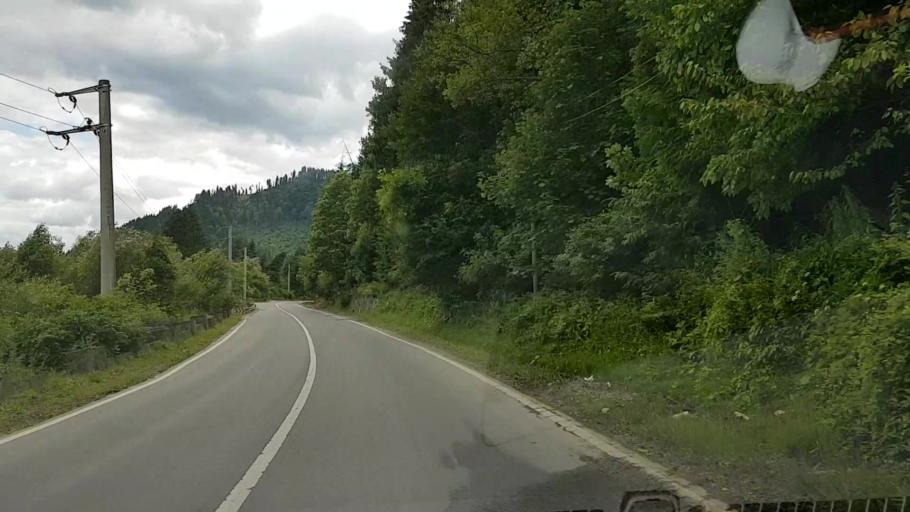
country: RO
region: Neamt
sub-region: Comuna Poiana Teiului
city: Poiana Teiului
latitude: 47.1024
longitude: 25.9401
